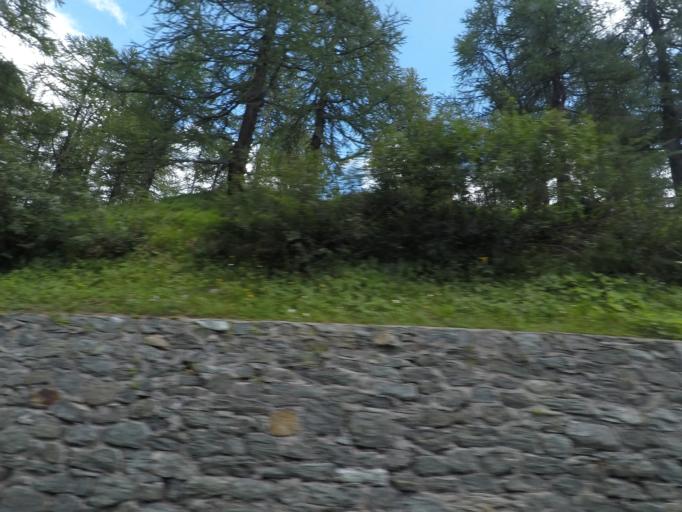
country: IT
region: Aosta Valley
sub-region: Valle d'Aosta
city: Paquier
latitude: 45.9248
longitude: 7.6196
